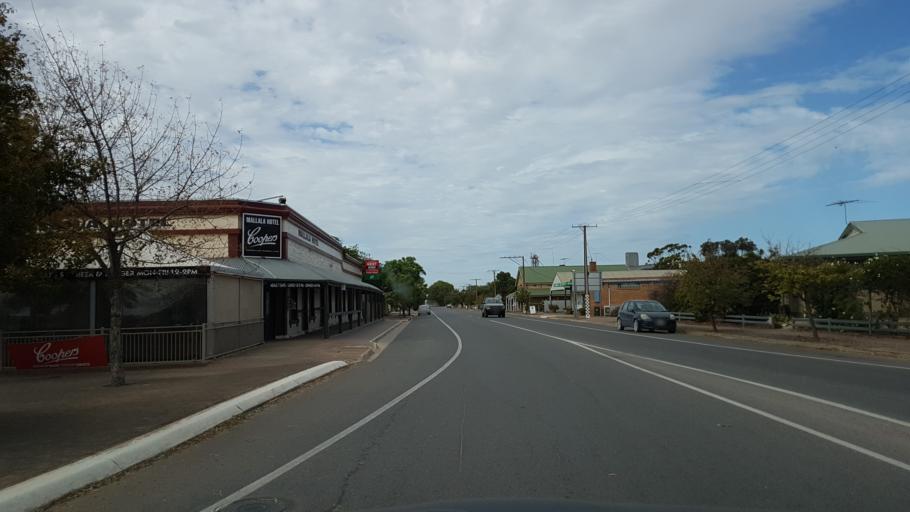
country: AU
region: South Australia
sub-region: Mallala
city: Mallala
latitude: -34.4380
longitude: 138.5099
